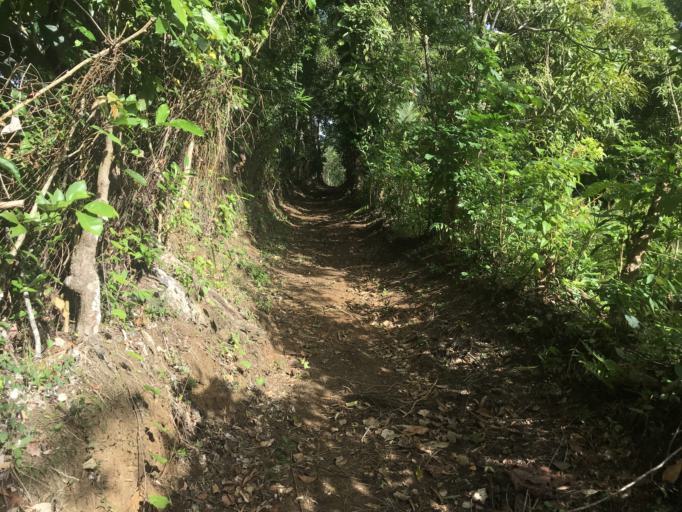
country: MQ
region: Martinique
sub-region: Martinique
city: Fort-de-France
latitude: 14.6503
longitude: -61.1093
